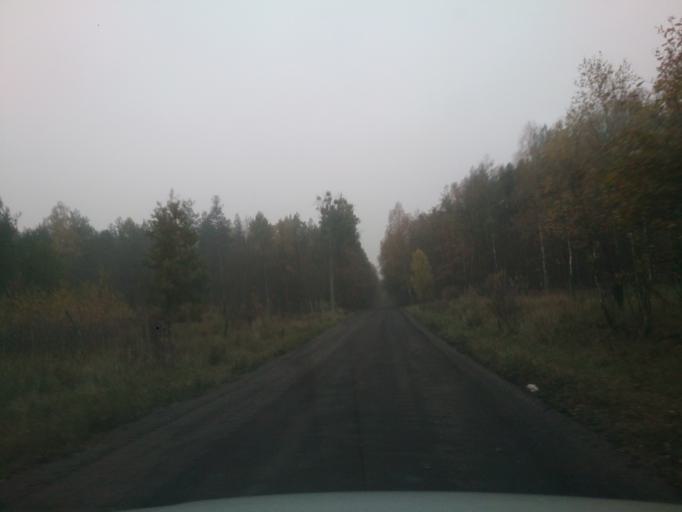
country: PL
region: Kujawsko-Pomorskie
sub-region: Powiat golubsko-dobrzynski
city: Golub-Dobrzyn
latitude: 53.1549
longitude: 19.1287
